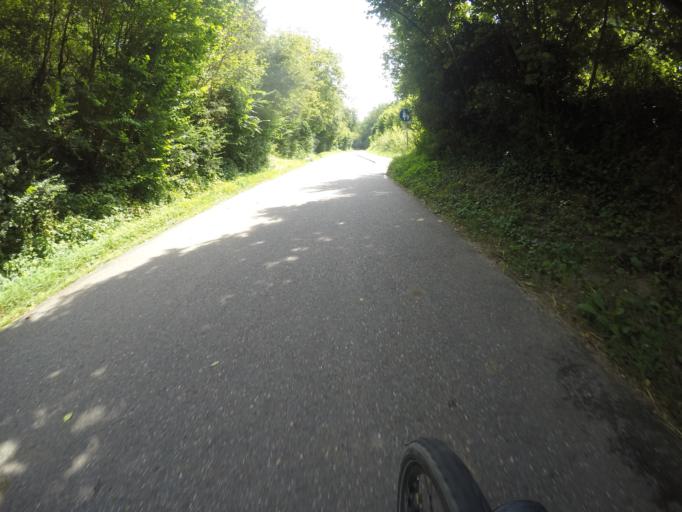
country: DE
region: Baden-Wuerttemberg
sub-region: Karlsruhe Region
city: Bruchsal
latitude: 49.1093
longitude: 8.6018
